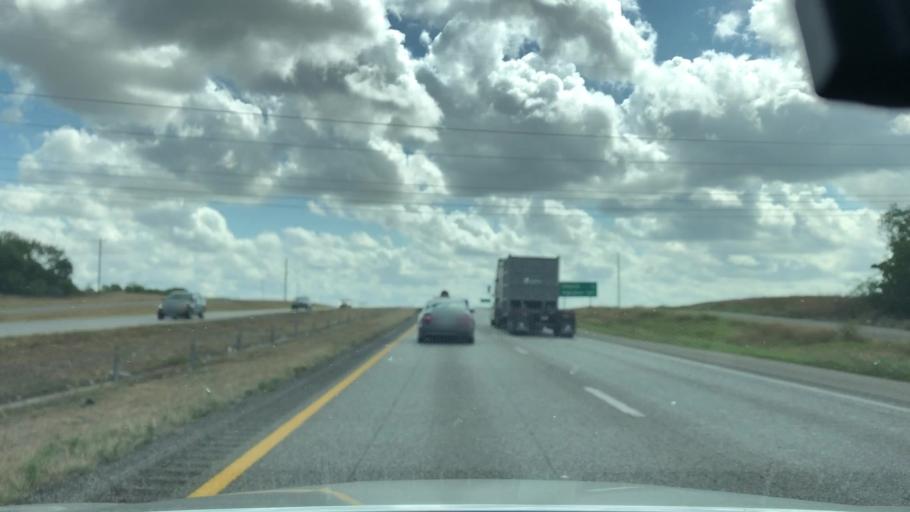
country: US
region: Texas
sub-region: Guadalupe County
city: McQueeney
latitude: 29.5443
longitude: -98.0604
